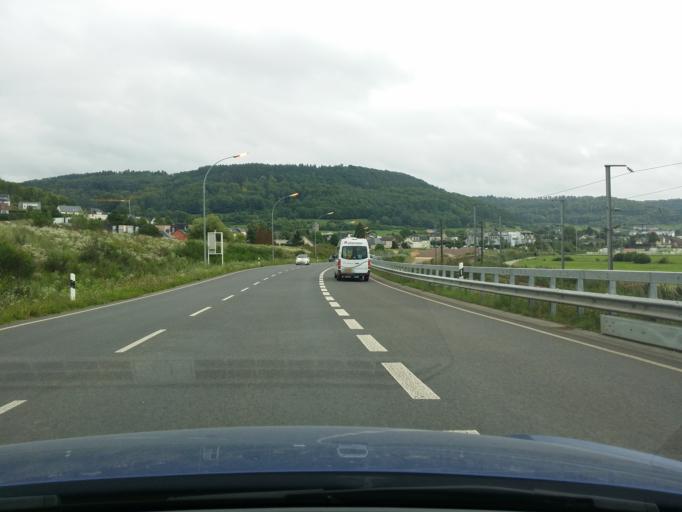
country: LU
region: Luxembourg
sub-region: Canton de Mersch
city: Lintgen
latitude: 49.7055
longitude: 6.1368
